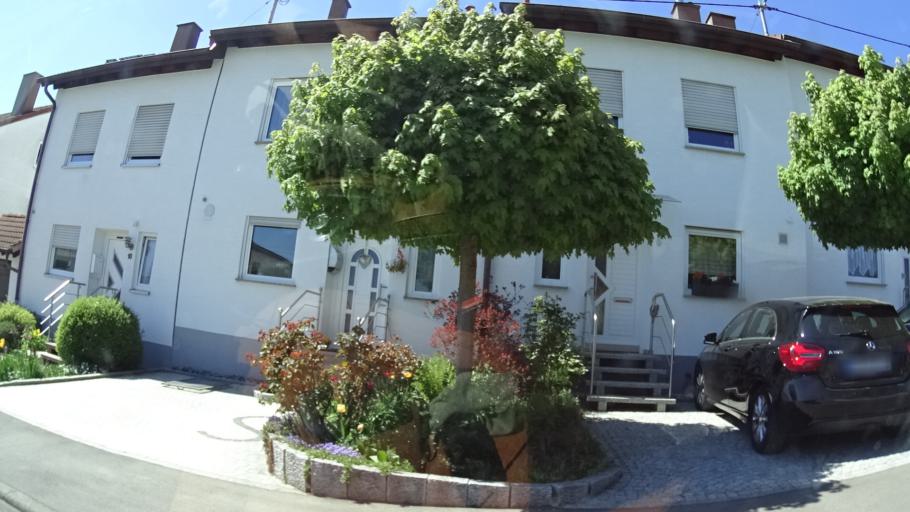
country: DE
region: Baden-Wuerttemberg
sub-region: Freiburg Region
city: Zimmern ob Rottweil
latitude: 48.1684
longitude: 8.5809
